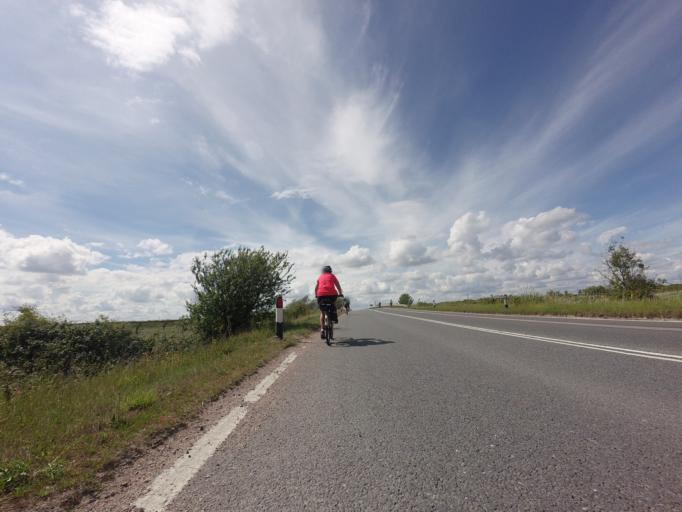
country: GB
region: England
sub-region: Medway
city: Allhallows
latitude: 51.4473
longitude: 0.6744
